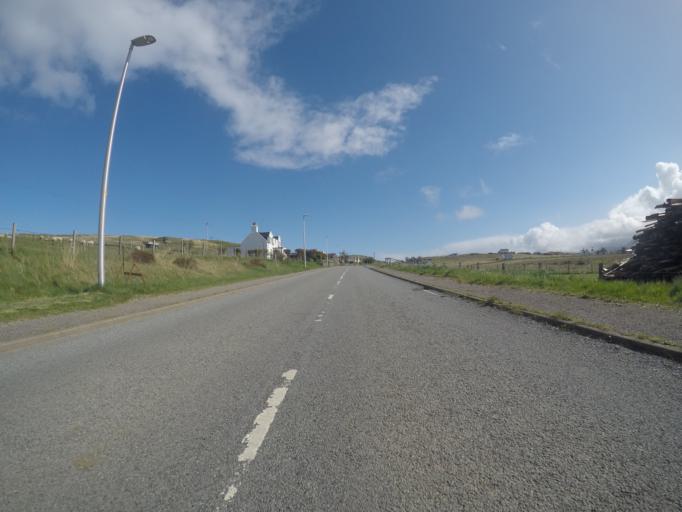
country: GB
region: Scotland
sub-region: Highland
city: Portree
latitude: 57.6248
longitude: -6.2036
